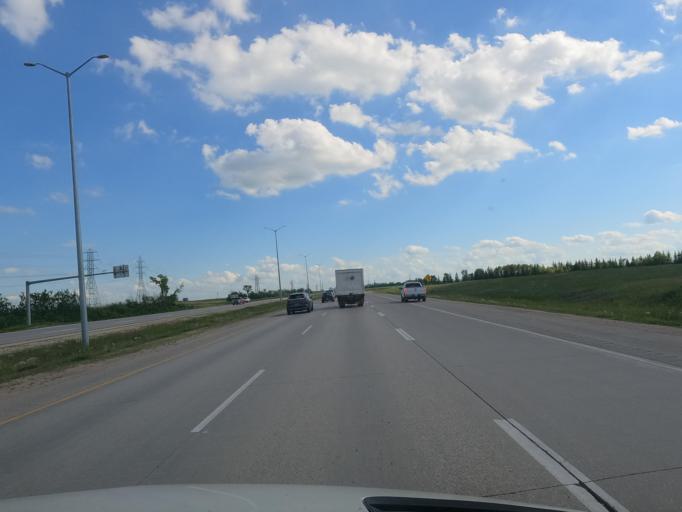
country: CA
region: Manitoba
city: Winnipeg
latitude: 49.8851
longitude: -96.9591
